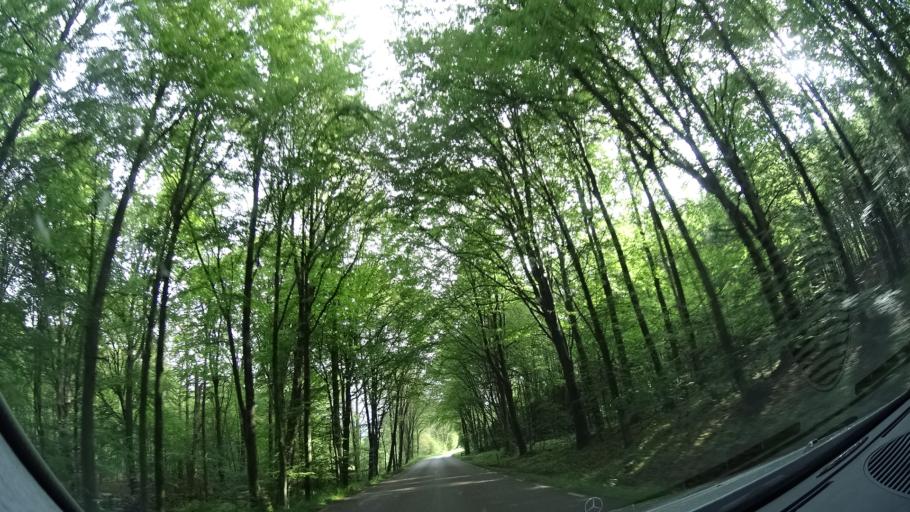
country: SE
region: Skane
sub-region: Hoors Kommun
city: Hoeoer
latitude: 55.9594
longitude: 13.4553
